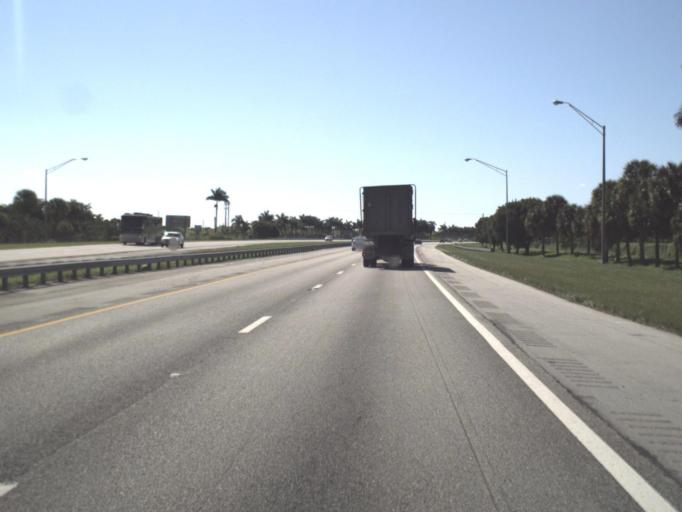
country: US
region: Florida
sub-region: Miami-Dade County
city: Goulds
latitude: 25.5472
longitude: -80.3629
